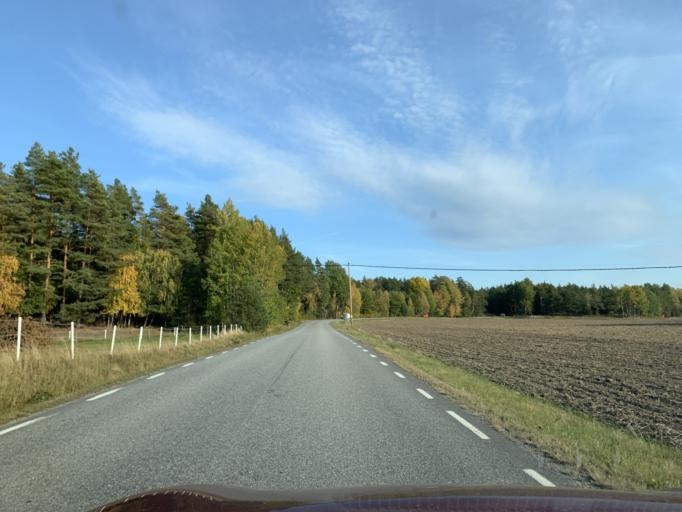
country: SE
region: Stockholm
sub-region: Upplands-Bro Kommun
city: Bro
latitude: 59.5079
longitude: 17.5997
